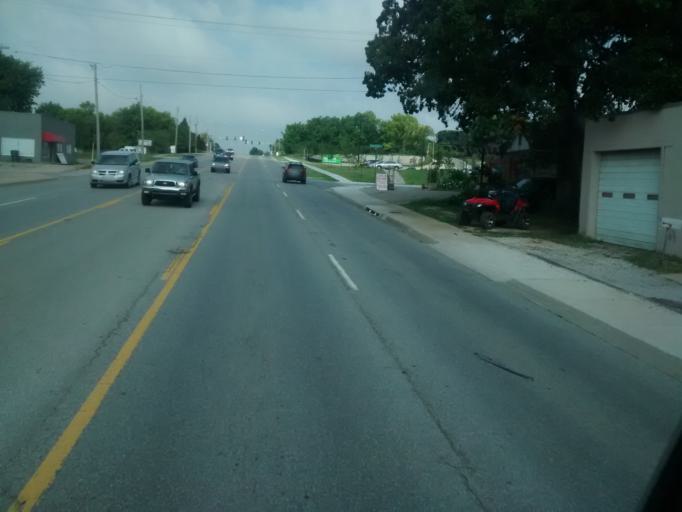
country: US
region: Arkansas
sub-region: Washington County
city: Fayetteville
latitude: 36.0566
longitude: -94.1672
